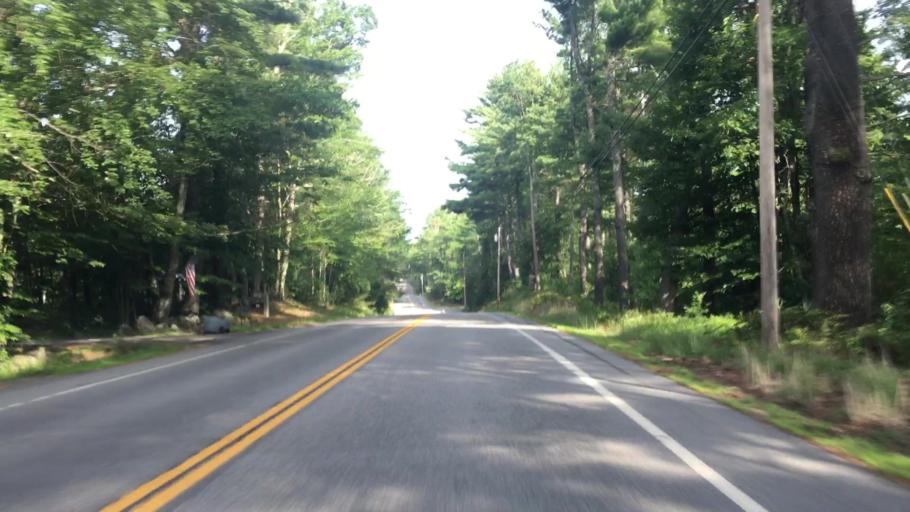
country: US
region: Maine
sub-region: York County
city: Limington
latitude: 43.7720
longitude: -70.7280
